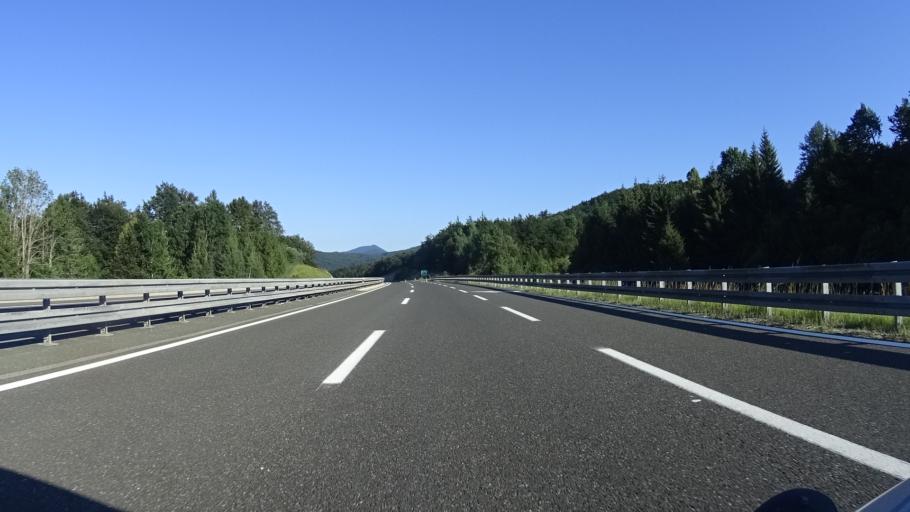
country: HR
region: Primorsko-Goranska
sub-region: Grad Delnice
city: Delnice
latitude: 45.3879
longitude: 14.8348
